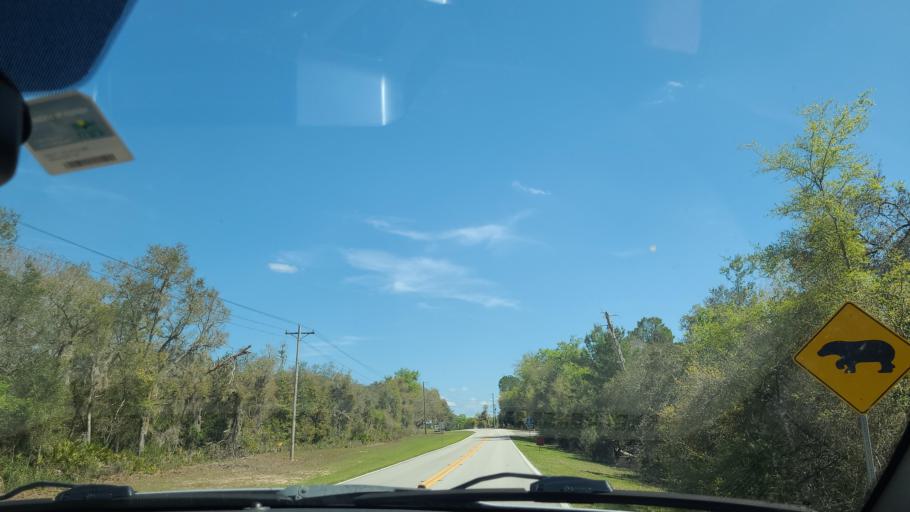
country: US
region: Florida
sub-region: Putnam County
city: Crescent City
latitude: 29.3758
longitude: -81.7516
